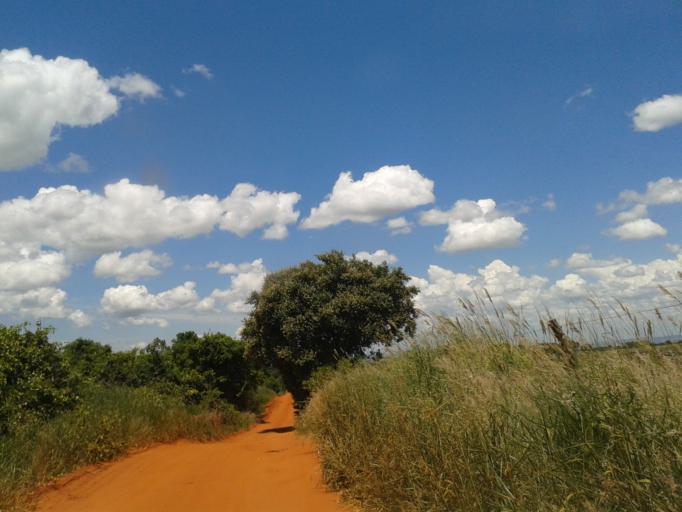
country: BR
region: Minas Gerais
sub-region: Centralina
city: Centralina
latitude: -18.6984
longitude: -49.1551
